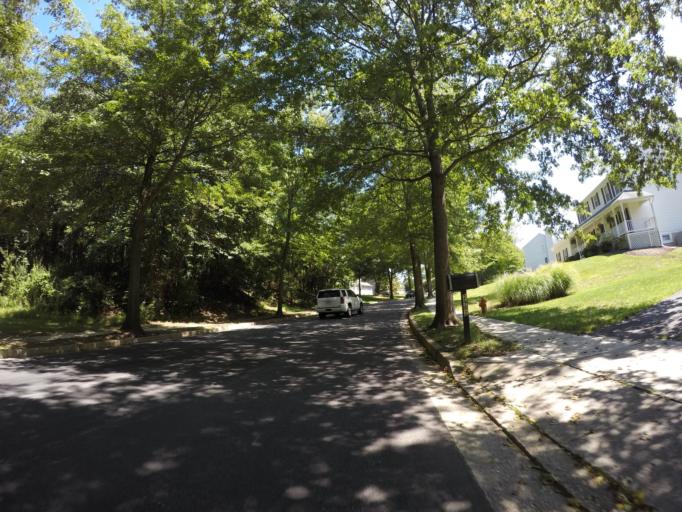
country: US
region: Maryland
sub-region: Howard County
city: Columbia
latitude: 39.2894
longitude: -76.8750
